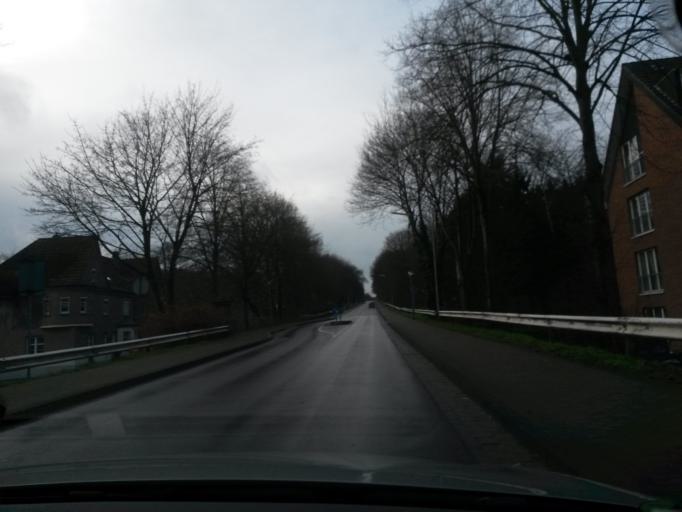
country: DE
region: North Rhine-Westphalia
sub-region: Regierungsbezirk Dusseldorf
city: Alpen
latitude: 51.5741
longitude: 6.5091
